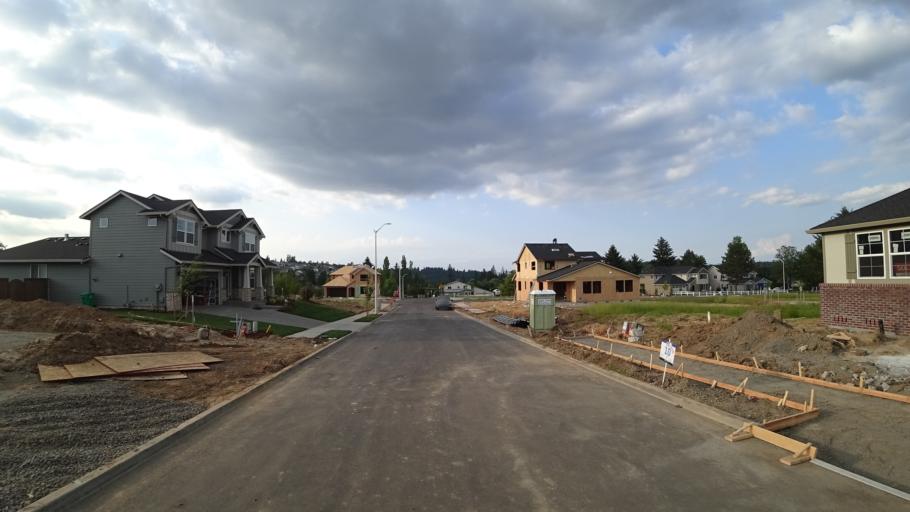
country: US
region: Oregon
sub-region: Clackamas County
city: Happy Valley
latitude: 45.4633
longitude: -122.4987
